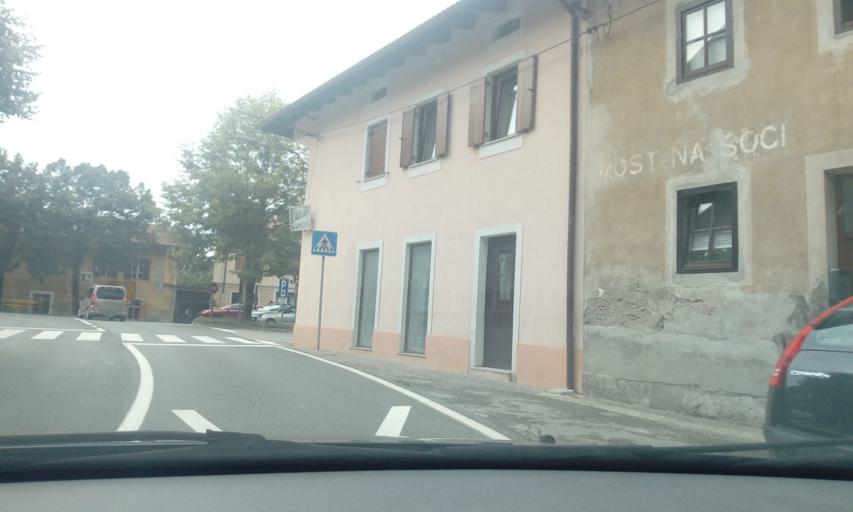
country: SI
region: Tolmin
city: Tolmin
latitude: 46.1528
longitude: 13.7419
